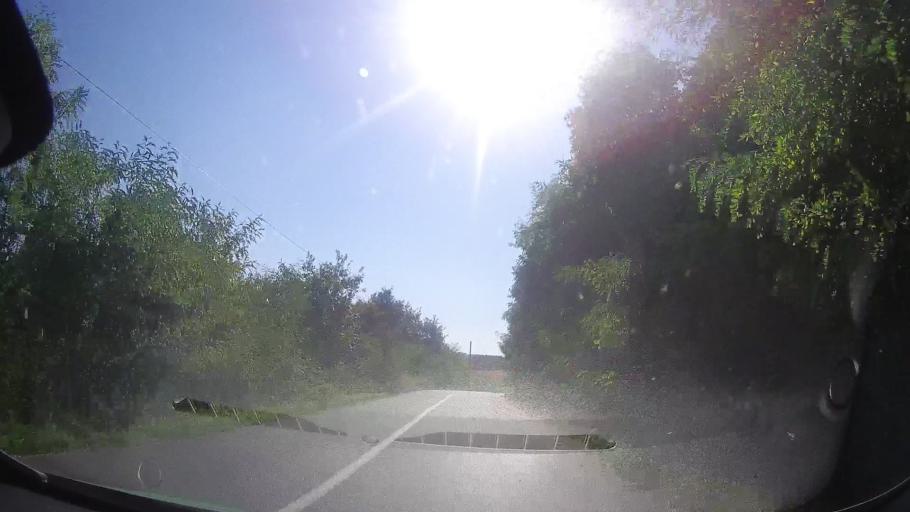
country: RO
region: Timis
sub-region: Comuna Ohaba Lunga
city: Ohaba Lunga
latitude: 45.8819
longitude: 21.9641
